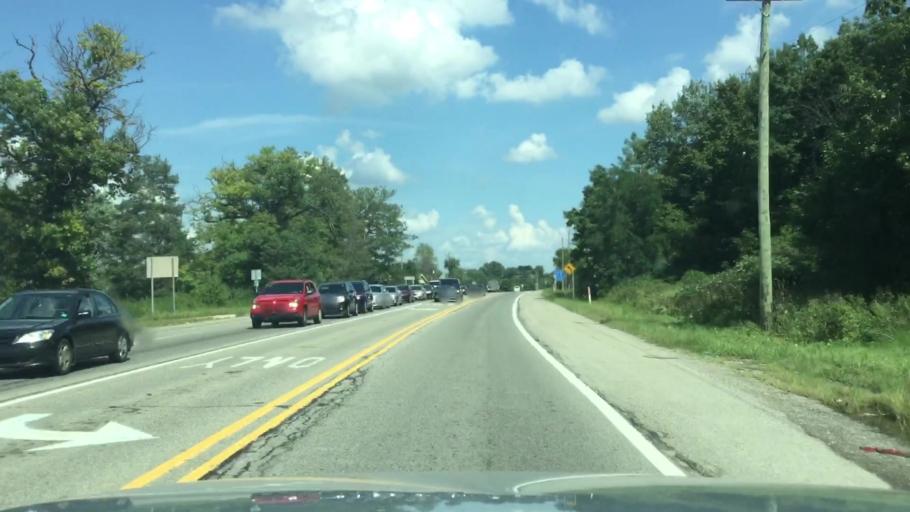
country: US
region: Michigan
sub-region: Washtenaw County
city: Ann Arbor
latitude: 42.1998
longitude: -83.6987
